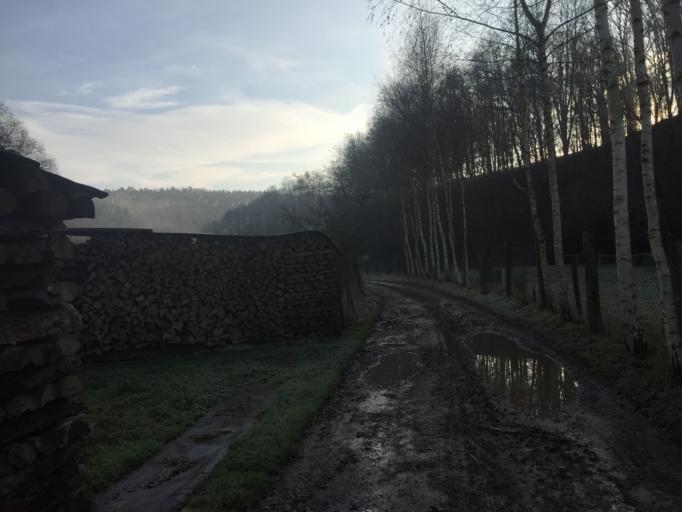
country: DE
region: Thuringia
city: Orlamunde
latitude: 50.7593
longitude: 11.5277
